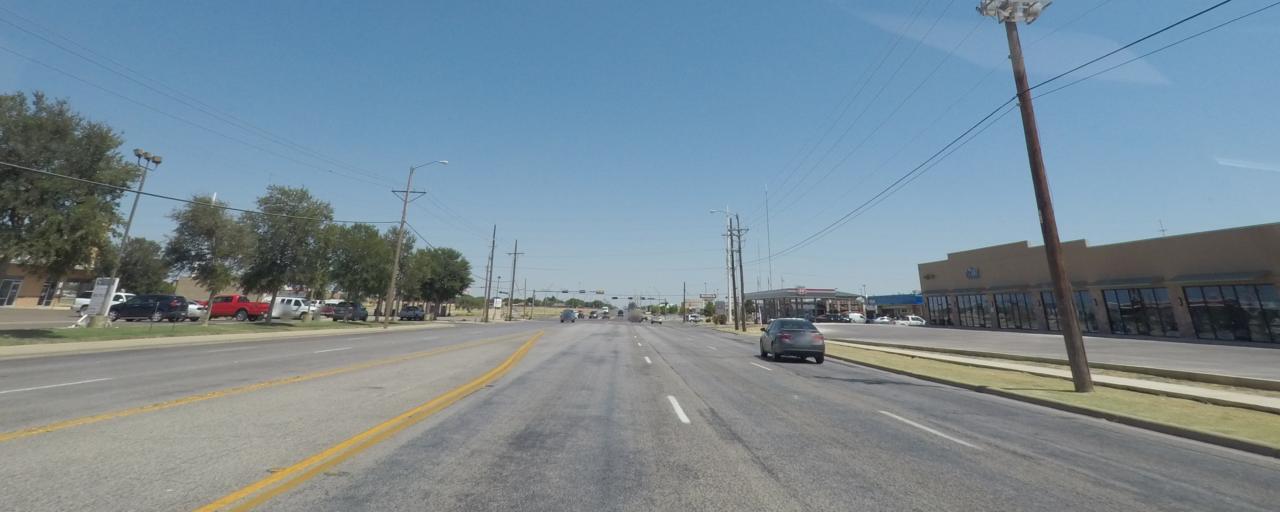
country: US
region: Texas
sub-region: Lubbock County
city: Lubbock
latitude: 33.5052
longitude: -101.8896
